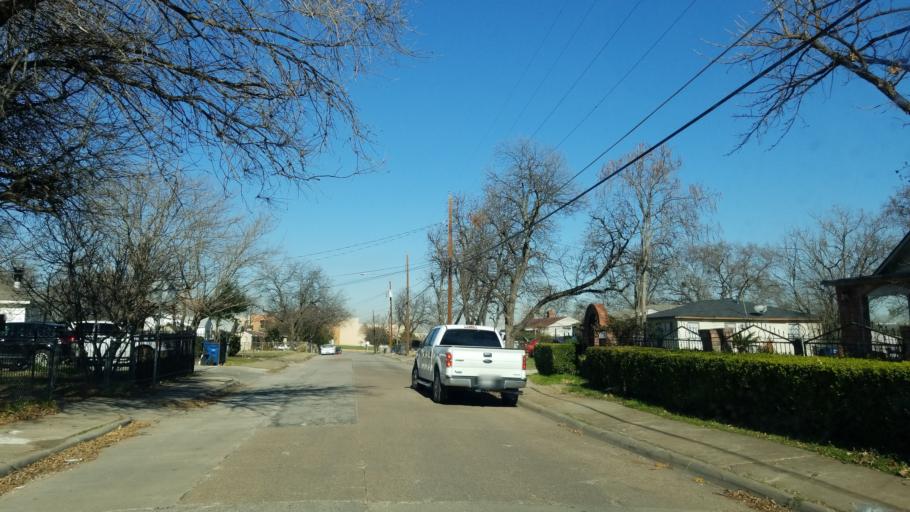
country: US
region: Texas
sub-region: Dallas County
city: Cockrell Hill
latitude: 32.7564
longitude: -96.9102
